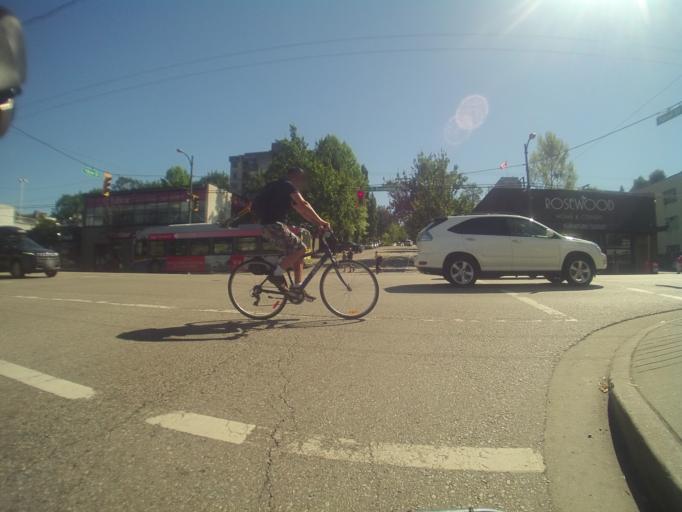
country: CA
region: British Columbia
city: Vancouver
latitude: 49.2634
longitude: -123.1130
